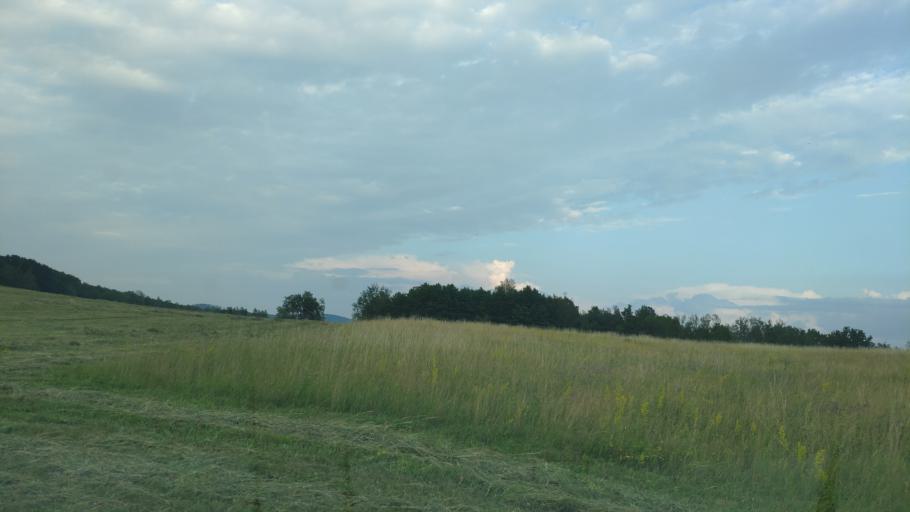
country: SK
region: Kosicky
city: Moldava nad Bodvou
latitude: 48.7154
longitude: 21.0011
